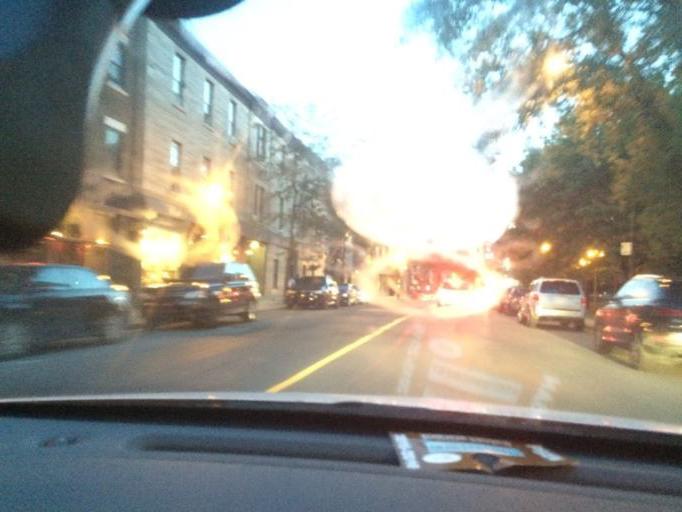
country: CA
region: Quebec
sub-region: Montreal
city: Montreal
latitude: 45.4874
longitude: -73.5691
